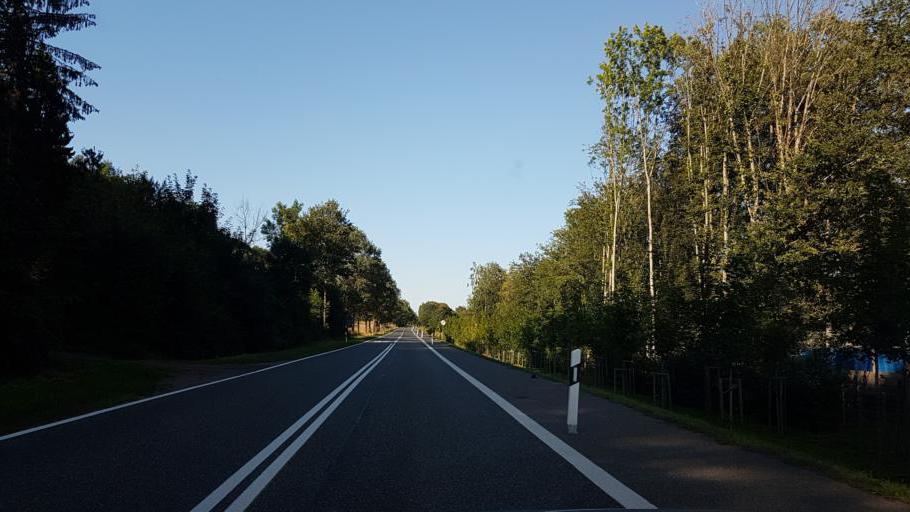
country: DE
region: Saarland
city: Weiskirchen
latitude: 49.5243
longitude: 6.8295
